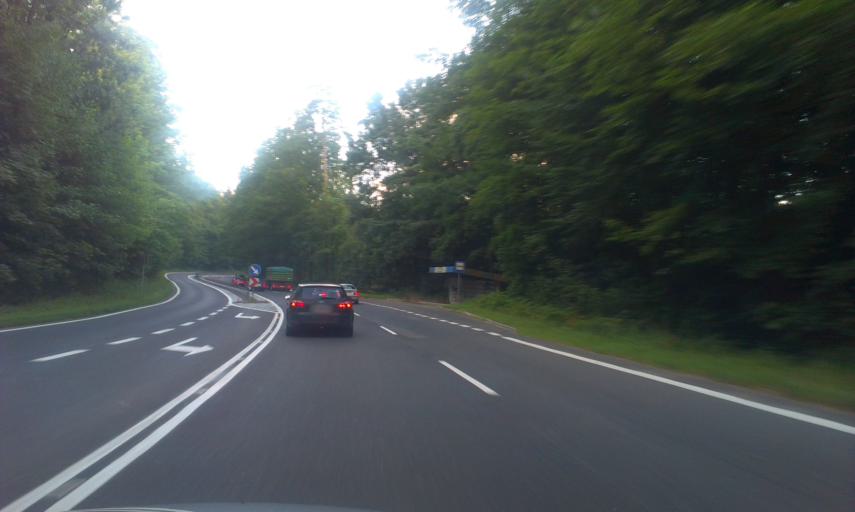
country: PL
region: West Pomeranian Voivodeship
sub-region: Koszalin
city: Koszalin
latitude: 54.2184
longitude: 16.2234
